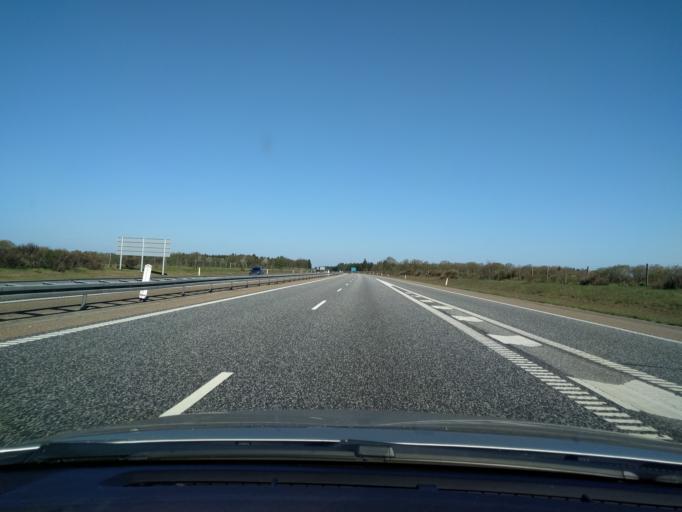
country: DK
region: Central Jutland
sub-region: Ikast-Brande Kommune
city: Brande
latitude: 55.9693
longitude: 9.0939
